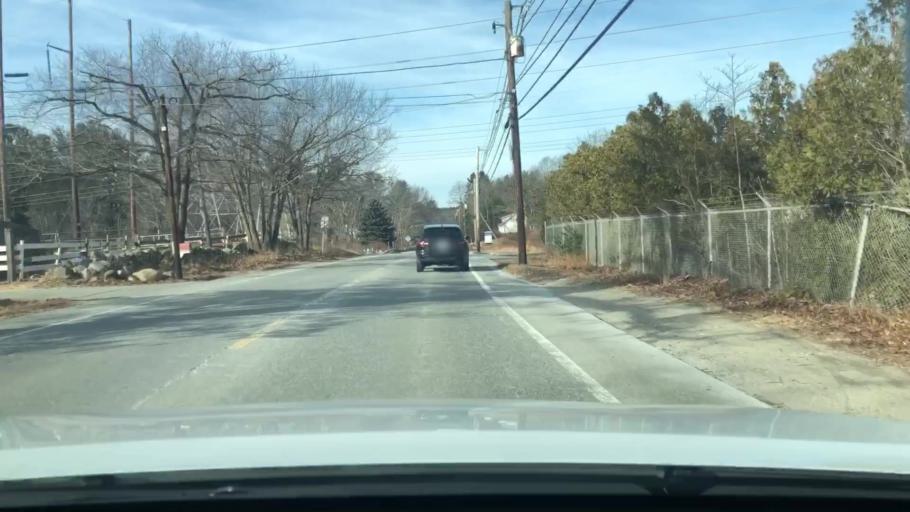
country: US
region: Massachusetts
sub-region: Worcester County
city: Northbridge
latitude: 42.1850
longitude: -71.6483
